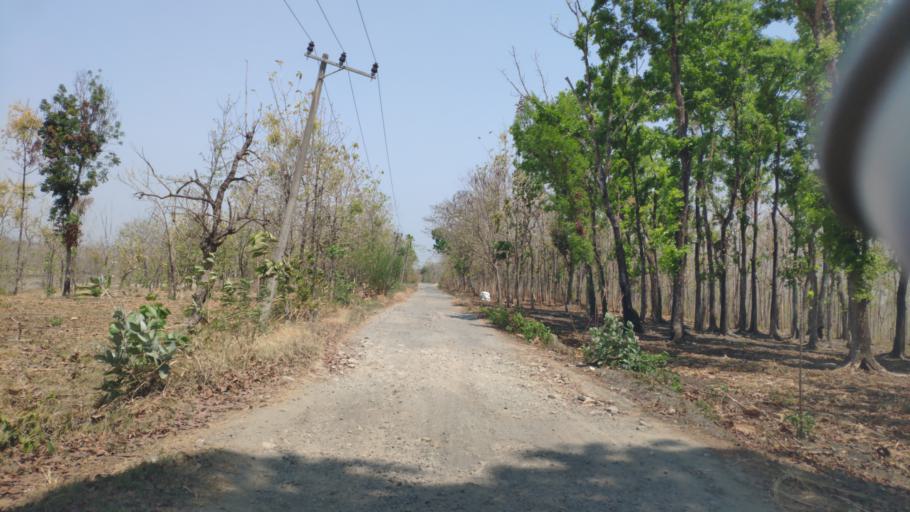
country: ID
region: West Java
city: Ngawi
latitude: -7.3503
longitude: 111.4294
